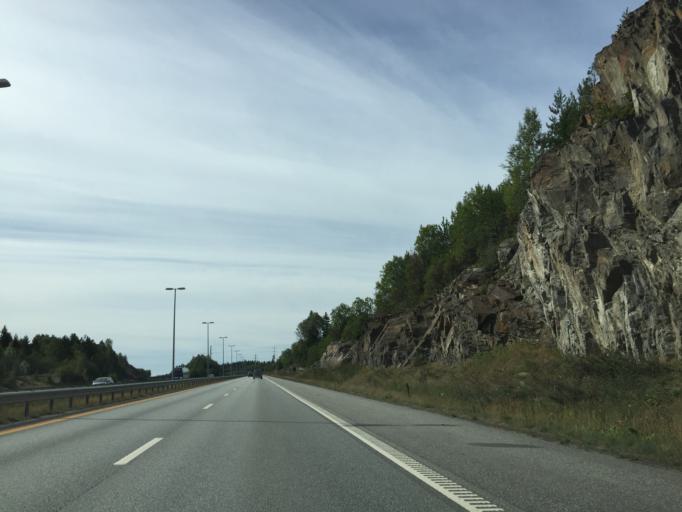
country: NO
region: Akershus
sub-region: Vestby
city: Vestby
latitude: 59.5766
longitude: 10.7277
